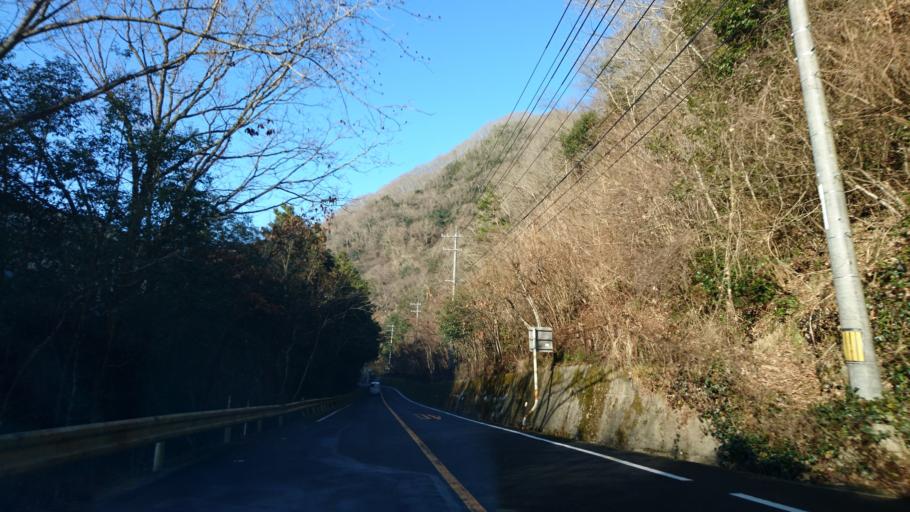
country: JP
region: Okayama
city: Takahashi
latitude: 34.8193
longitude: 133.6495
